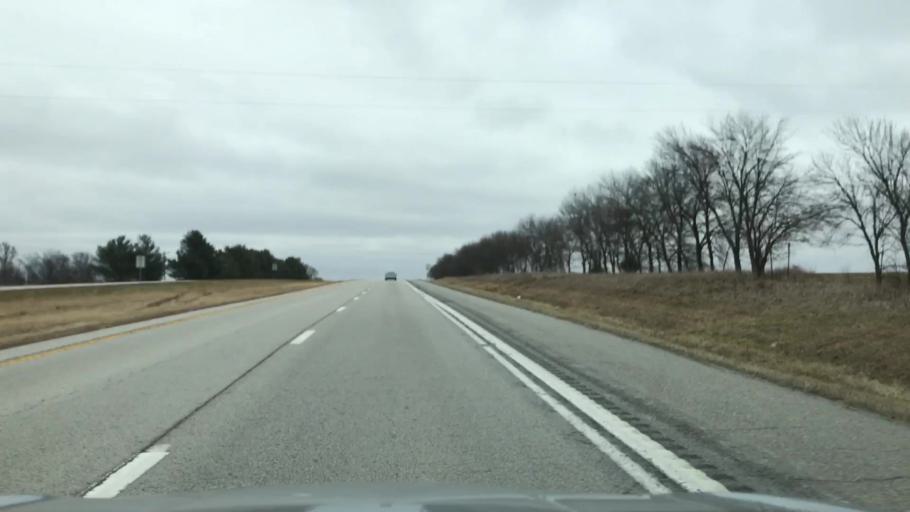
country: US
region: Missouri
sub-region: Livingston County
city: Chillicothe
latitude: 39.7771
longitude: -93.3835
